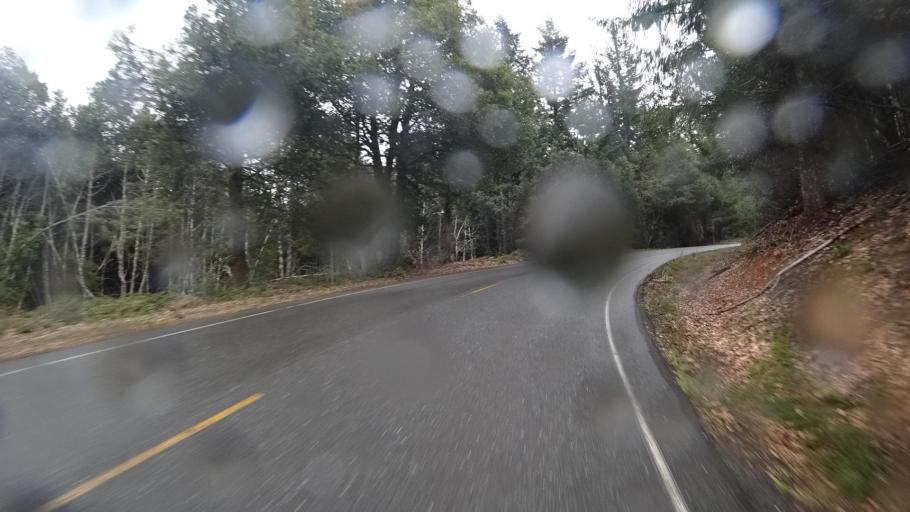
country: US
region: California
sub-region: Humboldt County
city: Willow Creek
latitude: 41.1621
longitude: -123.8179
